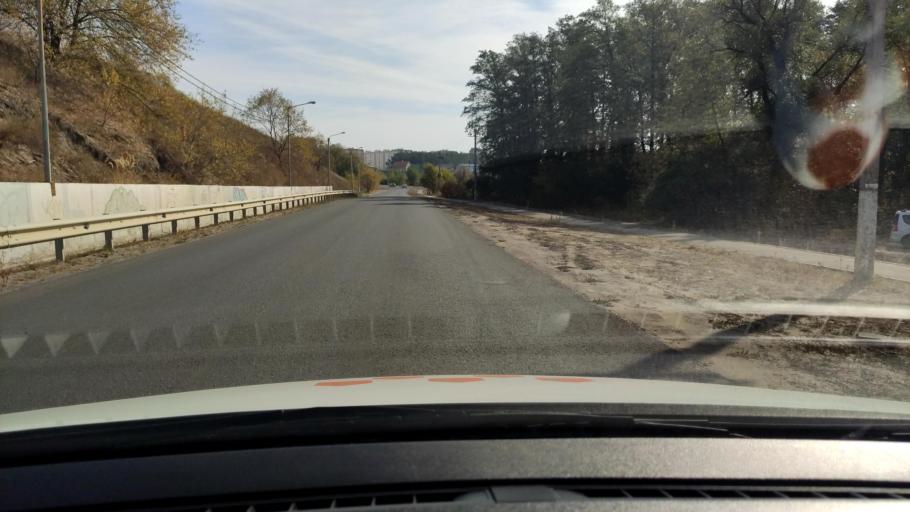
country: RU
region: Voronezj
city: Pridonskoy
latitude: 51.6645
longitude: 39.0886
